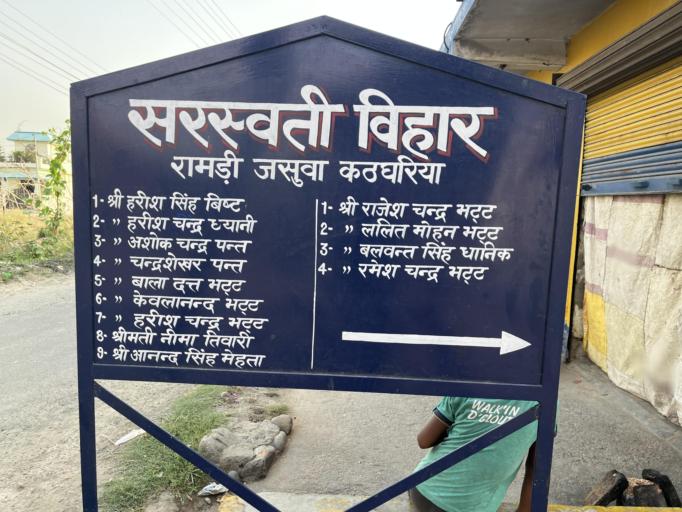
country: IN
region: Uttarakhand
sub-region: Naini Tal
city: Haldwani
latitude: 29.2333
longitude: 79.4701
